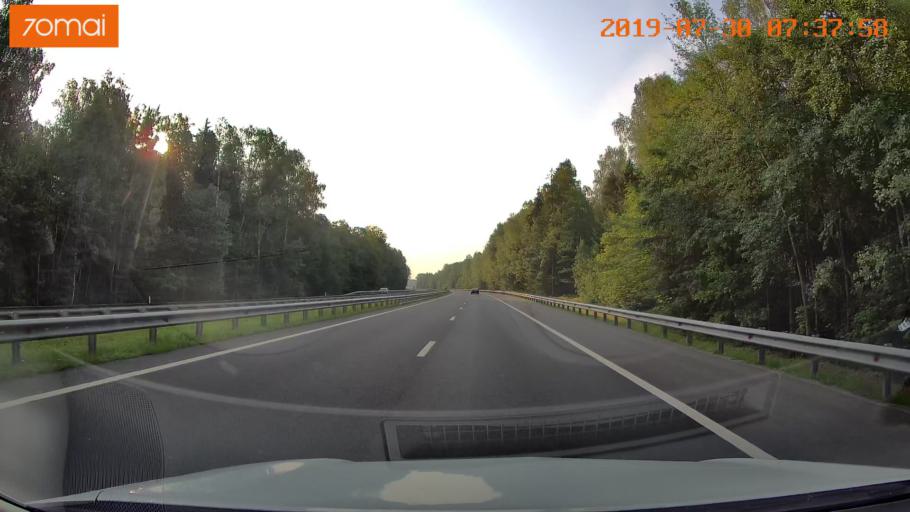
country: RU
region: Kaliningrad
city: Gvardeysk
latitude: 54.6522
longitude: 21.1564
